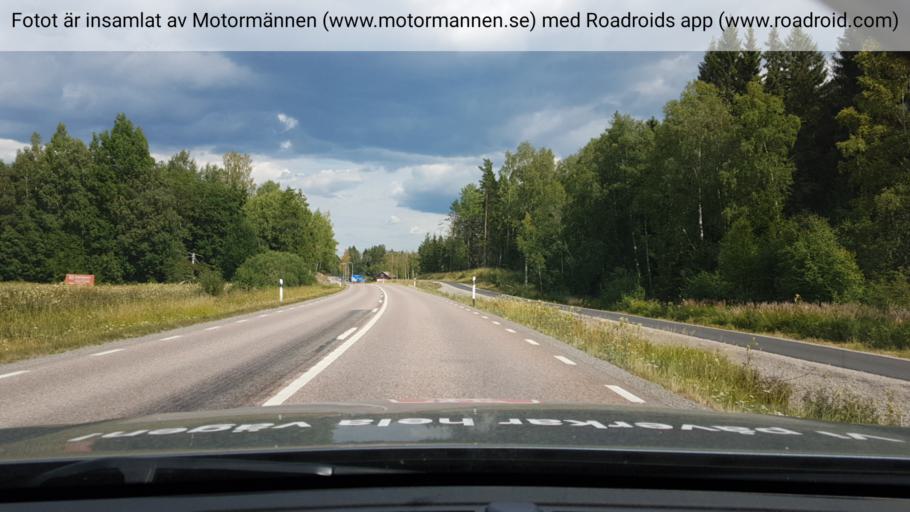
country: SE
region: Uppsala
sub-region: Heby Kommun
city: Morgongava
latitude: 59.9357
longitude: 16.9309
